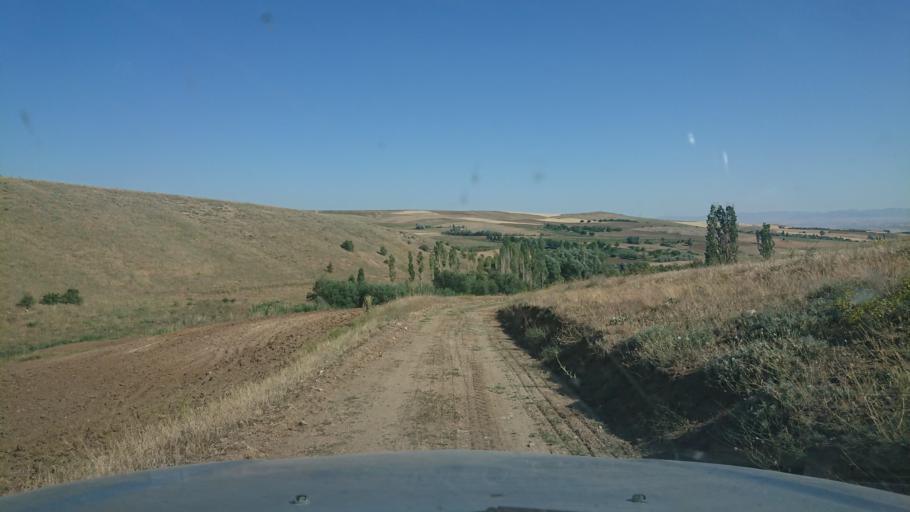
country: TR
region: Aksaray
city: Agacoren
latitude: 38.8383
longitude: 33.9261
